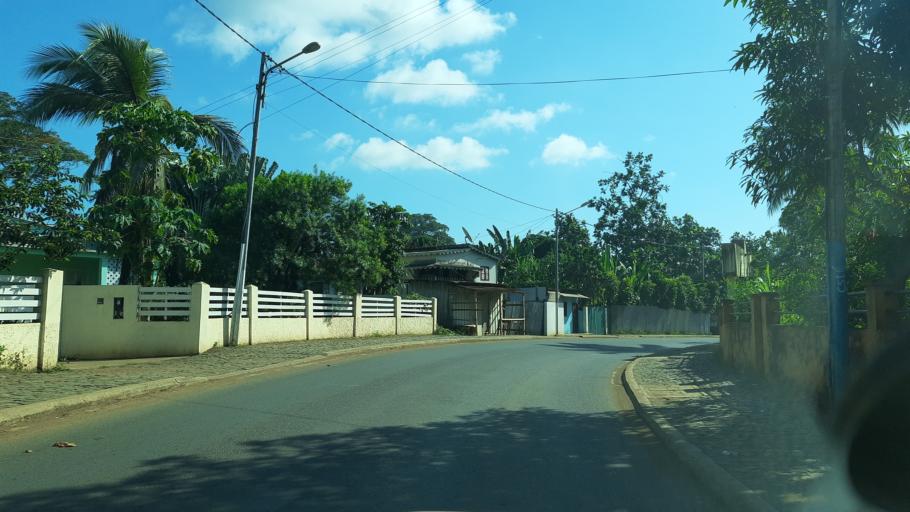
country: ST
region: Sao Tome Island
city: Sao Tome
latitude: 0.3265
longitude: 6.7277
